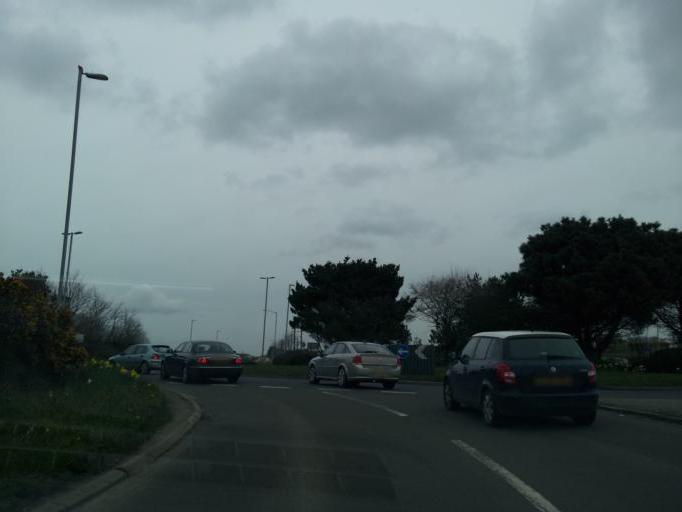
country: GB
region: England
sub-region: Cornwall
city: Redruth
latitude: 50.2425
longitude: -5.2336
